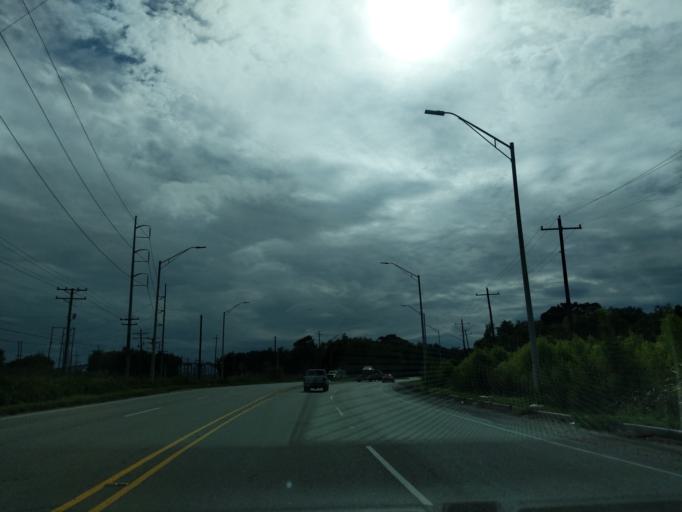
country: US
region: Louisiana
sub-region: Saint Bernard Parish
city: Chalmette
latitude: 30.0182
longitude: -89.9311
